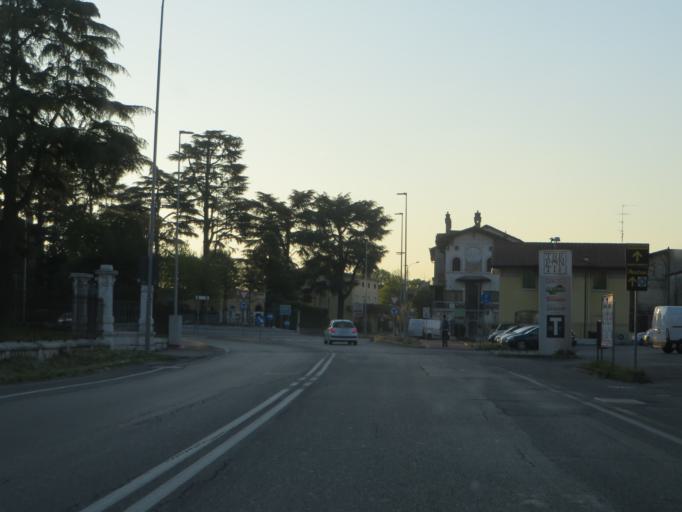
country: IT
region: Lombardy
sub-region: Provincia di Brescia
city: Rezzato
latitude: 45.5076
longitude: 10.3306
